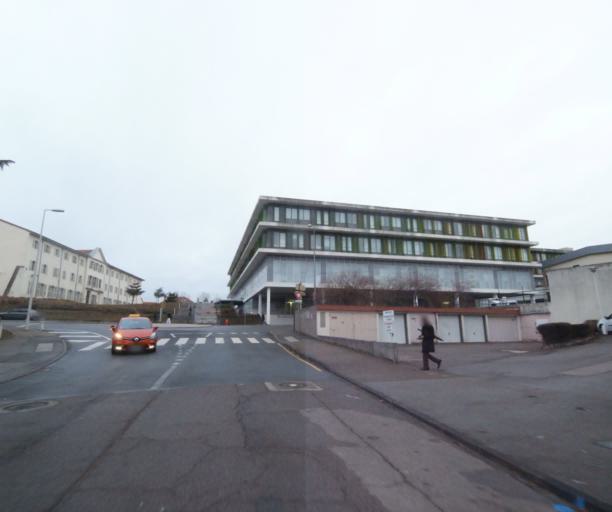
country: FR
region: Rhone-Alpes
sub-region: Departement de la Loire
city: Roanne
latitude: 46.0413
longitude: 4.0782
